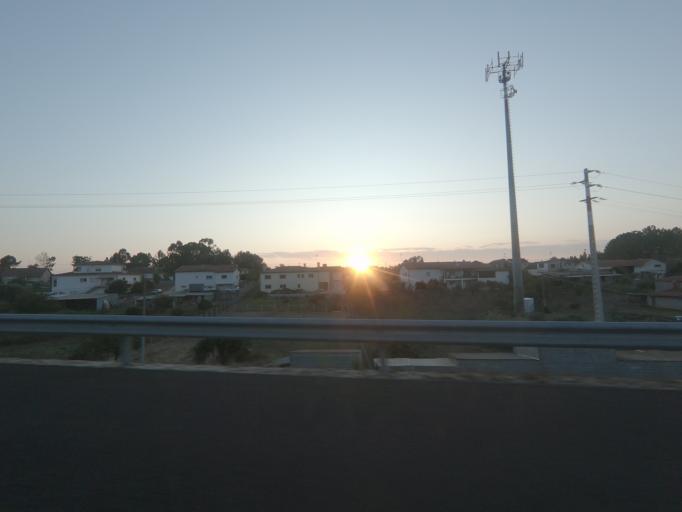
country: PT
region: Leiria
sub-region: Pombal
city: Pombal
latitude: 39.9024
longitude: -8.6895
